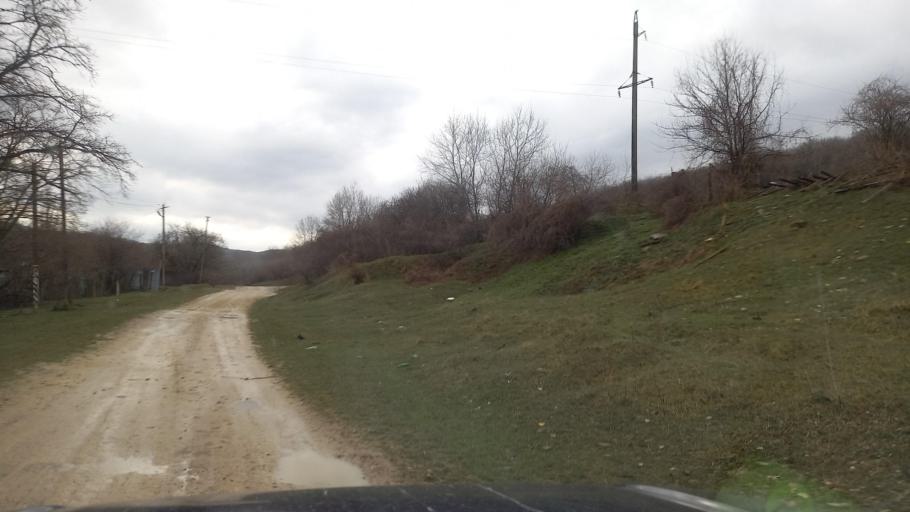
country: RU
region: Krasnodarskiy
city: Krymsk
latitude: 44.8601
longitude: 37.8491
